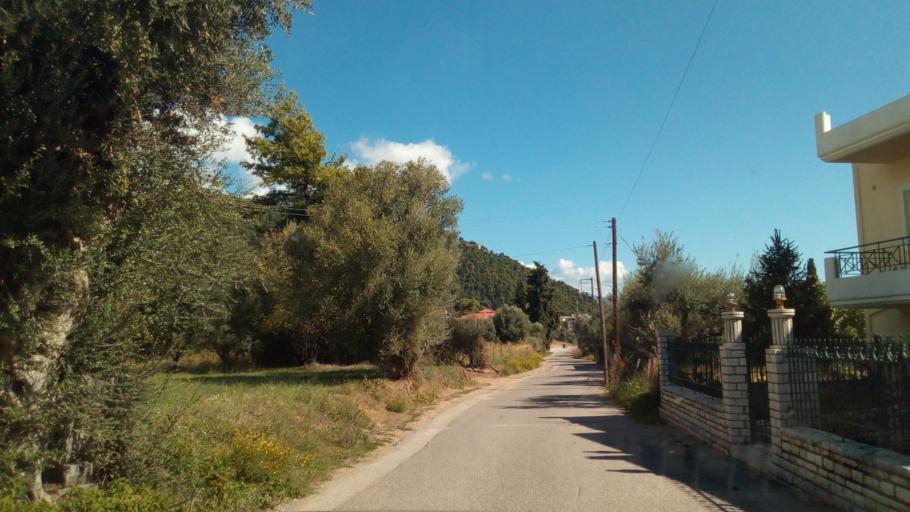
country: GR
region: West Greece
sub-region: Nomos Aitolias kai Akarnanias
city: Nafpaktos
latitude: 38.3918
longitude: 21.8119
